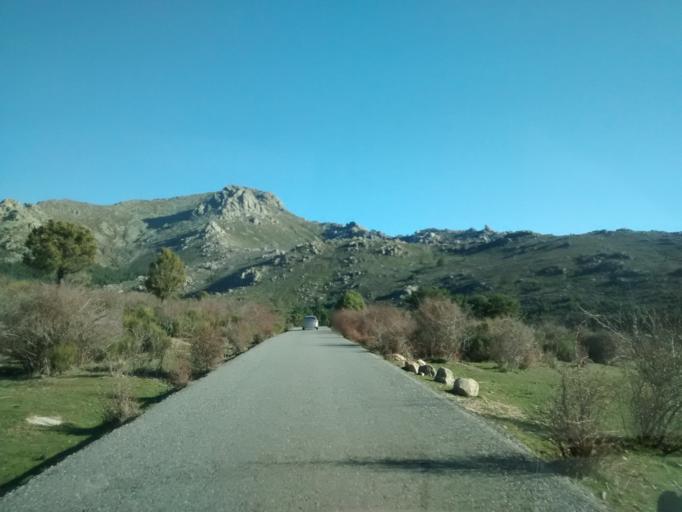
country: ES
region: Madrid
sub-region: Provincia de Madrid
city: Navacerrada
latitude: 40.7455
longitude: -3.9975
